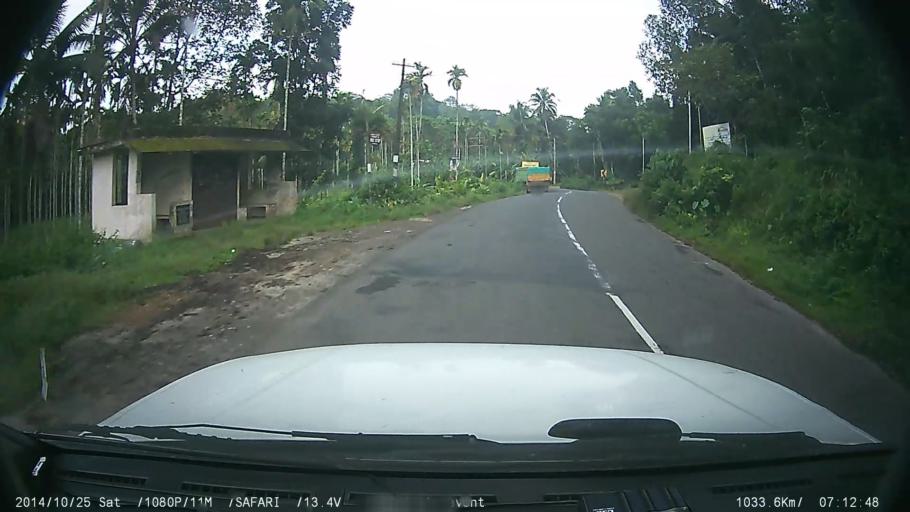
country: IN
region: Kerala
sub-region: Kottayam
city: Palackattumala
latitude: 9.8276
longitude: 76.5905
